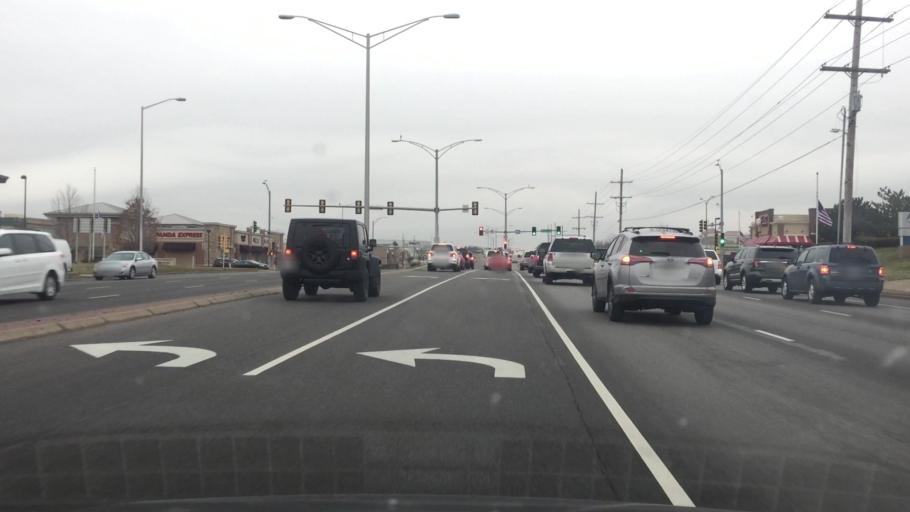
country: US
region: Kansas
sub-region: Johnson County
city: Lenexa
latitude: 38.8837
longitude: -94.6728
